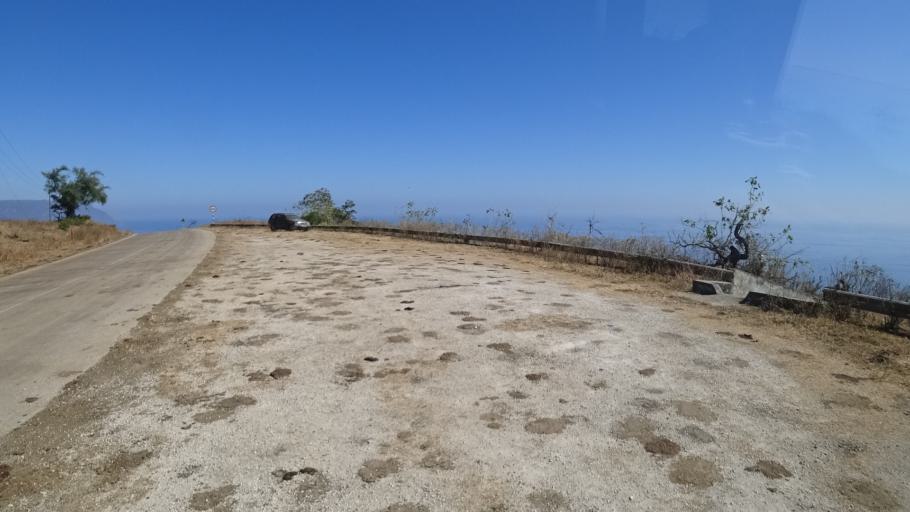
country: YE
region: Al Mahrah
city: Hawf
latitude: 16.7411
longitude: 53.3656
